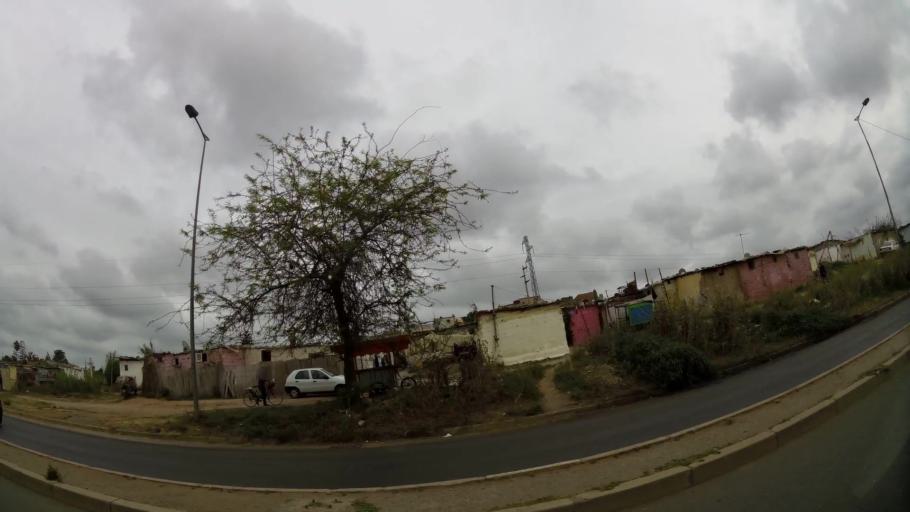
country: MA
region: Rabat-Sale-Zemmour-Zaer
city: Sale
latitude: 34.0399
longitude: -6.7978
